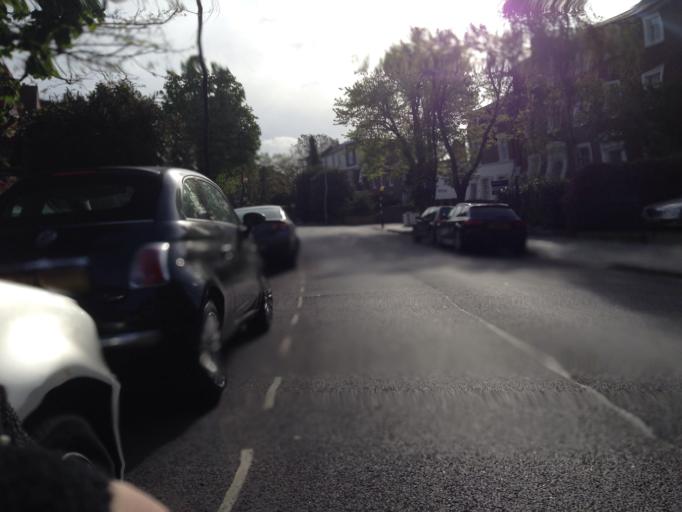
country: GB
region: England
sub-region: Greater London
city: Battersea
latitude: 51.4680
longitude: -0.1386
